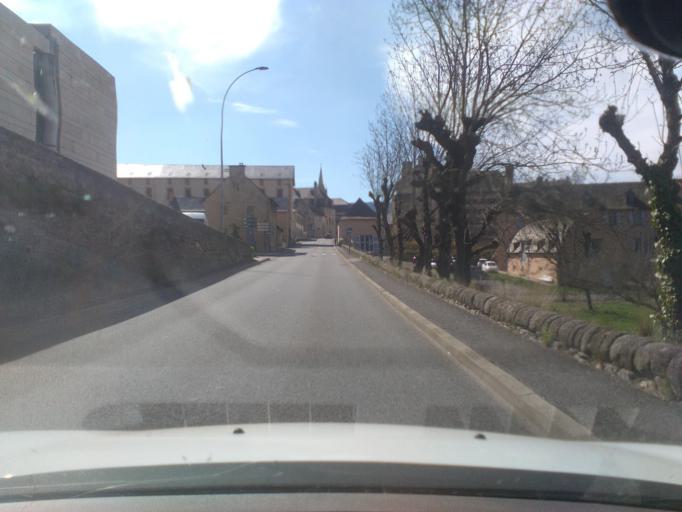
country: FR
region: Languedoc-Roussillon
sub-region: Departement de la Lozere
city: Mende
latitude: 44.5177
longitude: 3.5063
